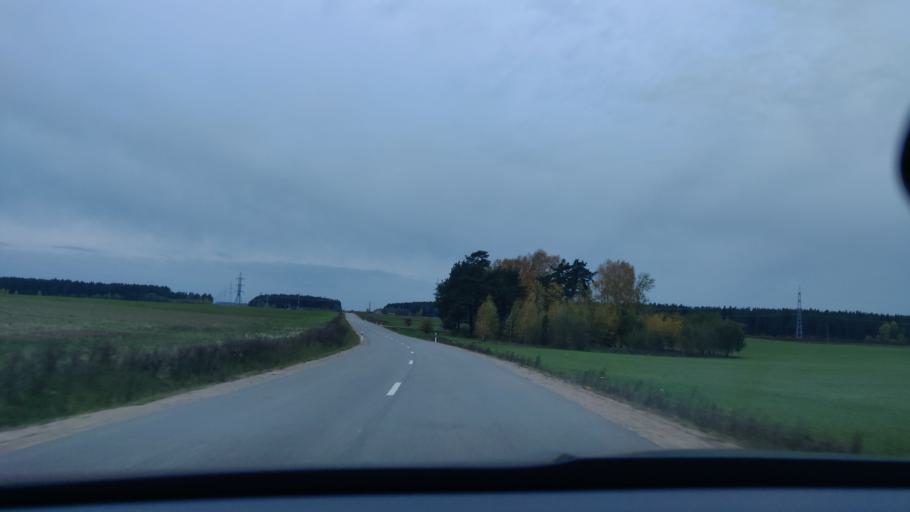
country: LT
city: Lentvaris
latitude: 54.5929
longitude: 25.0452
